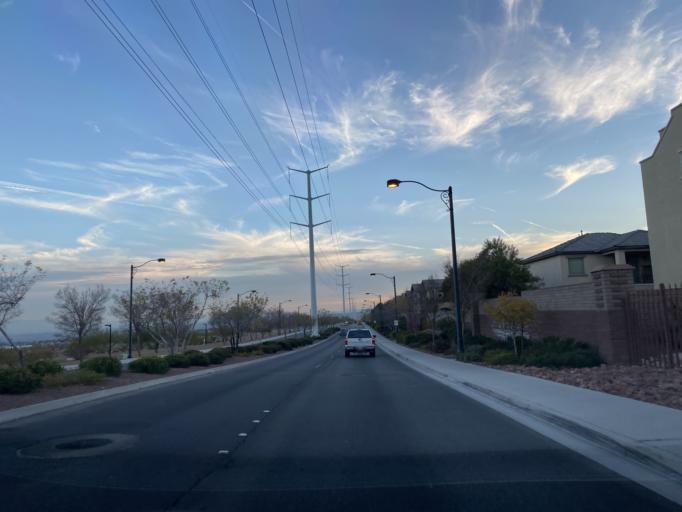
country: US
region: Nevada
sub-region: Clark County
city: Summerlin South
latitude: 36.2866
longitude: -115.3290
